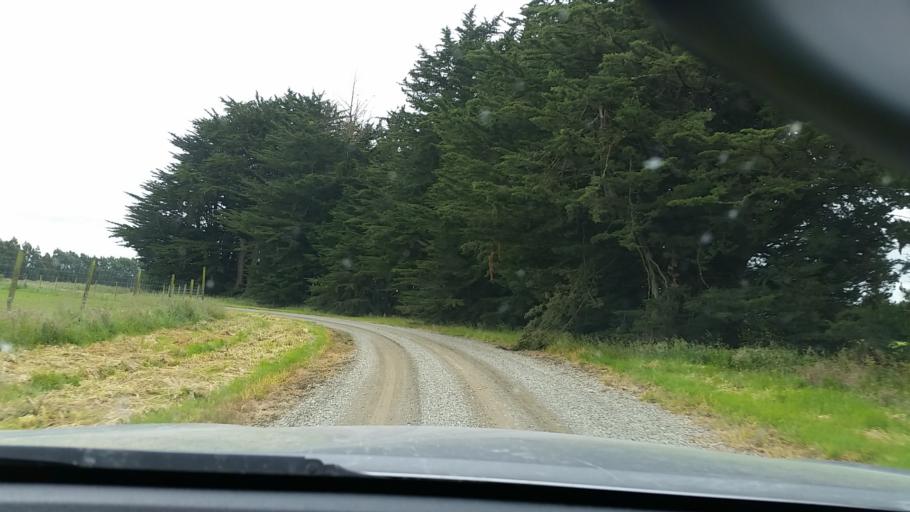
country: NZ
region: Southland
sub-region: Southland District
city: Winton
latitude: -46.1966
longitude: 168.2923
